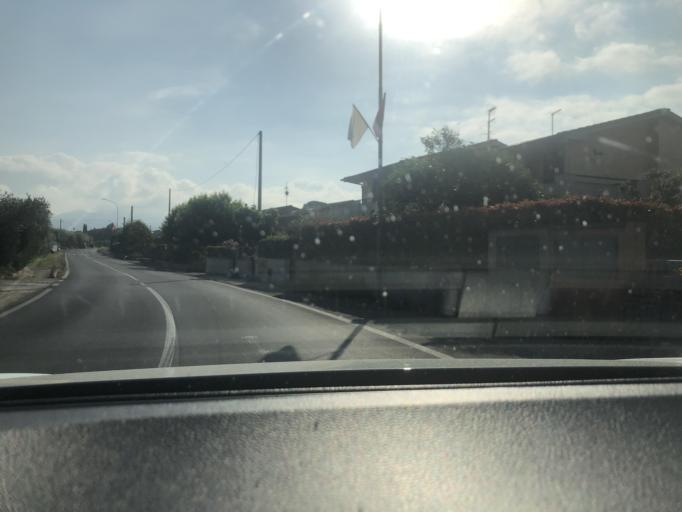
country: IT
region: Tuscany
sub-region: Province of Florence
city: Lazzeretto
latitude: 43.8029
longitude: 10.8553
